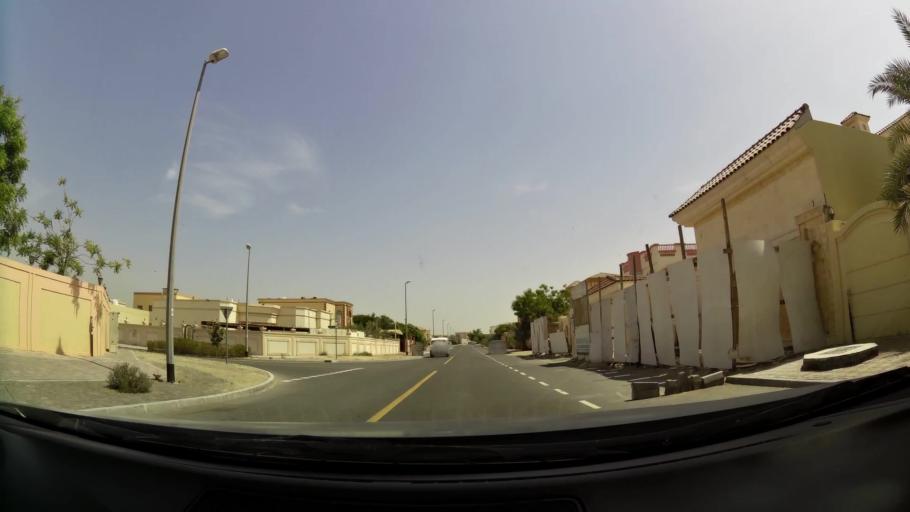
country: AE
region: Ash Shariqah
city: Sharjah
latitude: 25.1857
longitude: 55.4266
